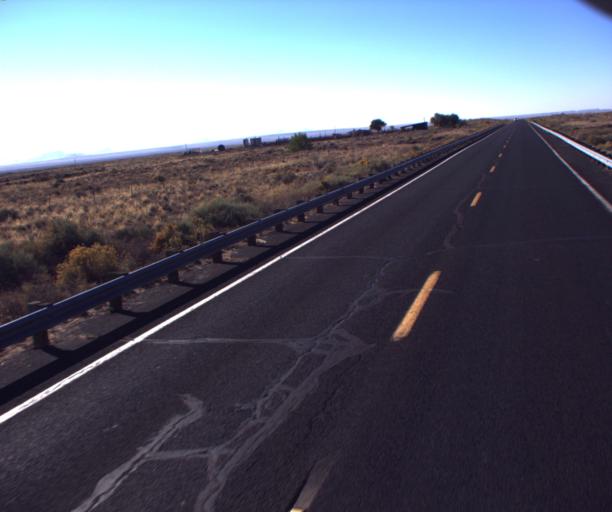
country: US
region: Arizona
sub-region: Navajo County
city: First Mesa
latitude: 35.7747
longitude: -110.5044
